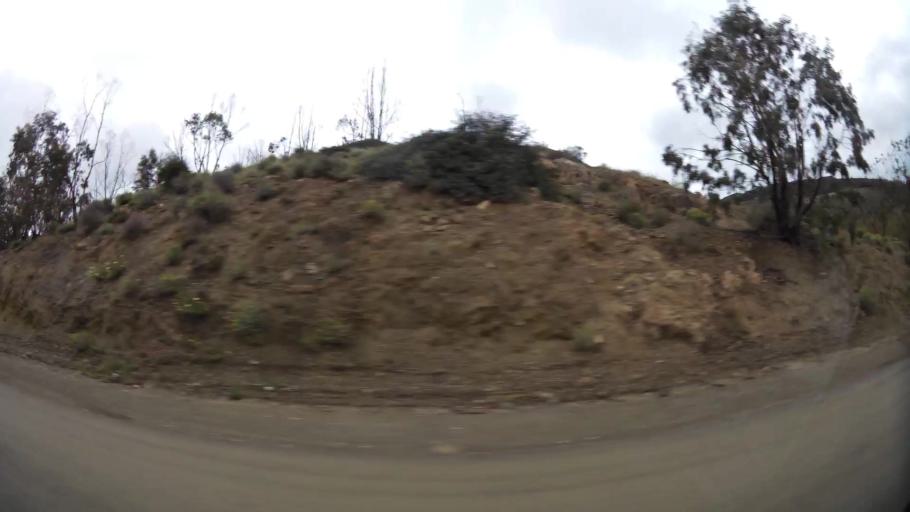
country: MA
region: Taza-Al Hoceima-Taounate
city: Imzourene
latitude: 34.9379
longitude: -3.8101
